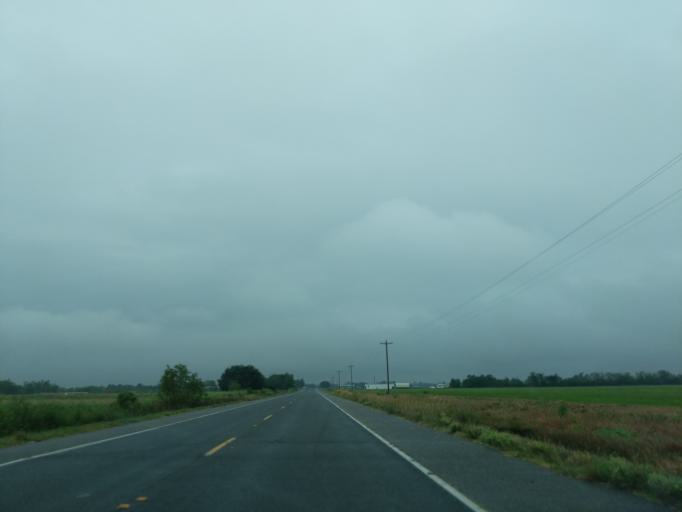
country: US
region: Louisiana
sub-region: Vermilion Parish
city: Kaplan
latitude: 29.9915
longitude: -92.2536
